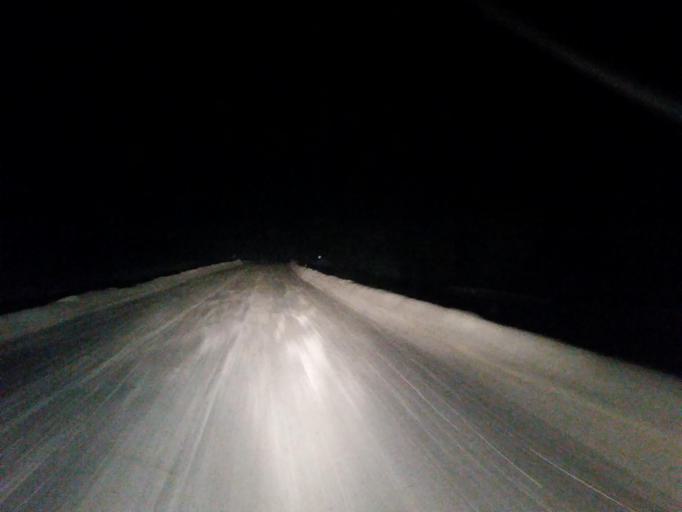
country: SE
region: Norrbotten
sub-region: Pitea Kommun
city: Roknas
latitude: 65.5213
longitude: 21.2018
